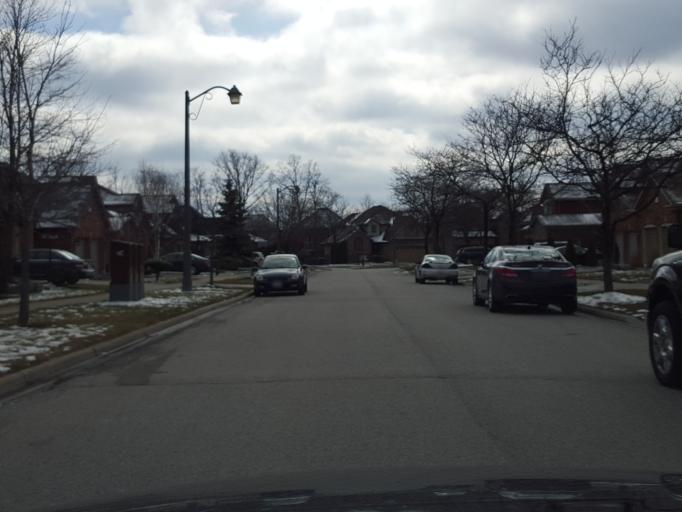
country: CA
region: Ontario
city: Burlington
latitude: 43.3873
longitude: -79.7999
